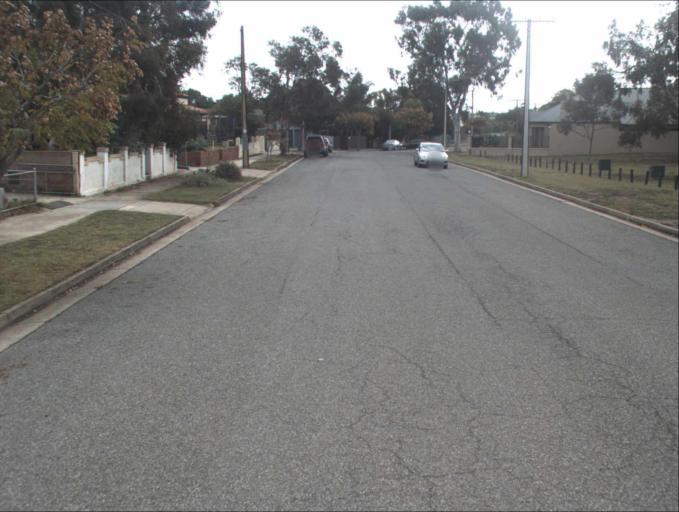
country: AU
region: South Australia
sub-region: Charles Sturt
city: West Lakes Shore
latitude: -34.8472
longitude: 138.4828
